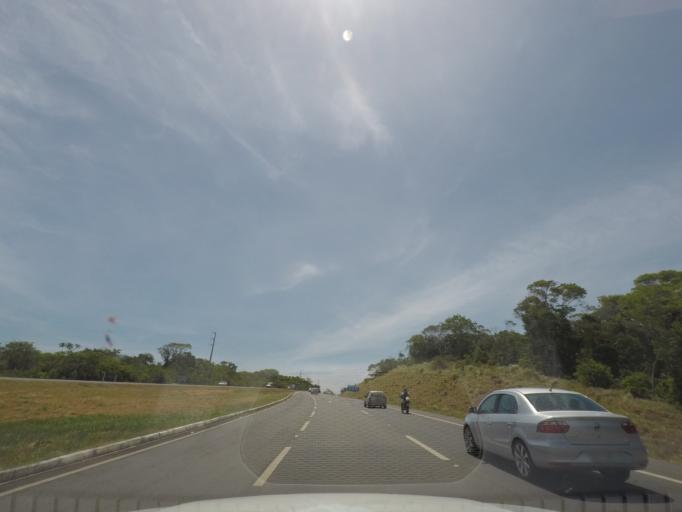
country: BR
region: Bahia
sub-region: Mata De Sao Joao
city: Mata de Sao Joao
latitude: -12.5664
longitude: -38.0276
